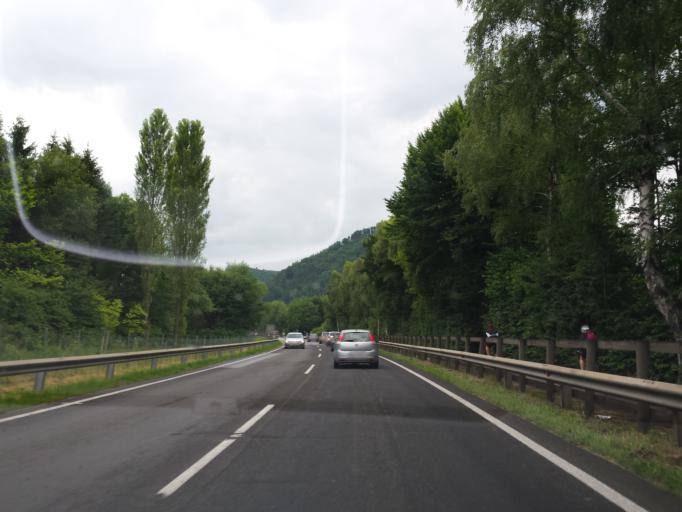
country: AT
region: Styria
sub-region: Graz Stadt
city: Goesting
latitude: 47.1079
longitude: 15.4104
